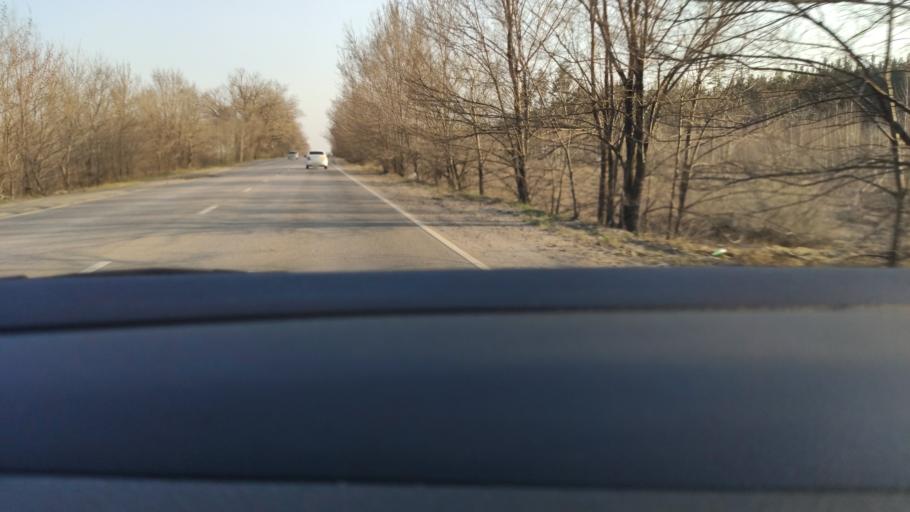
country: RU
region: Voronezj
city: Maslovka
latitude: 51.5627
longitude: 39.2747
